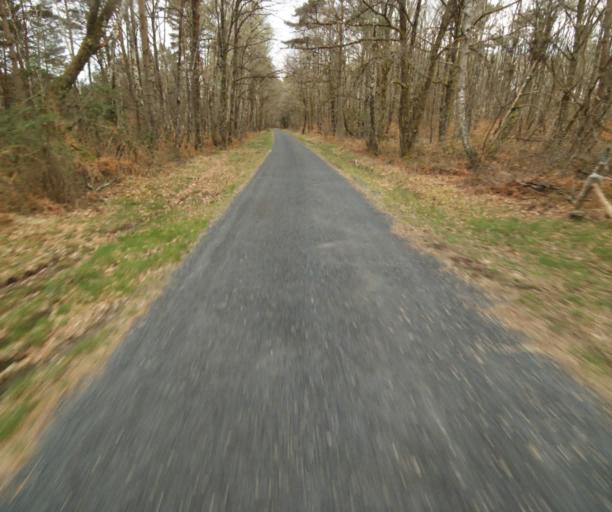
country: FR
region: Limousin
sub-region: Departement de la Correze
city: Saint-Privat
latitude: 45.1970
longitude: 1.9996
